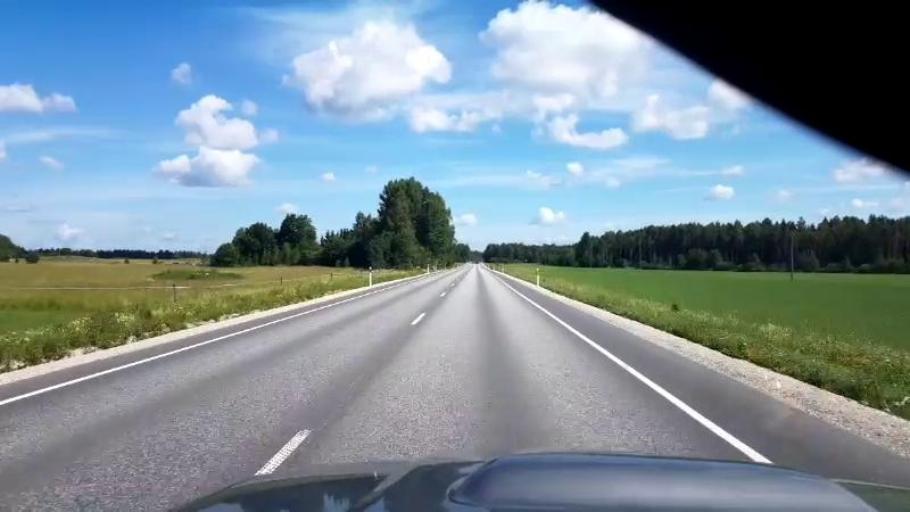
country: EE
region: Jaervamaa
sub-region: Paide linn
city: Paide
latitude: 58.9897
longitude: 25.6719
